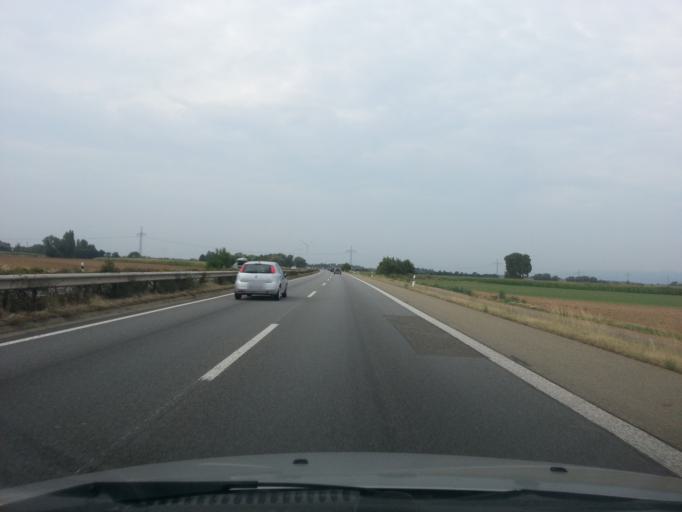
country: DE
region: Rheinland-Pfalz
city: Hochdorf-Assenheim
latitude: 49.4073
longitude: 8.2807
